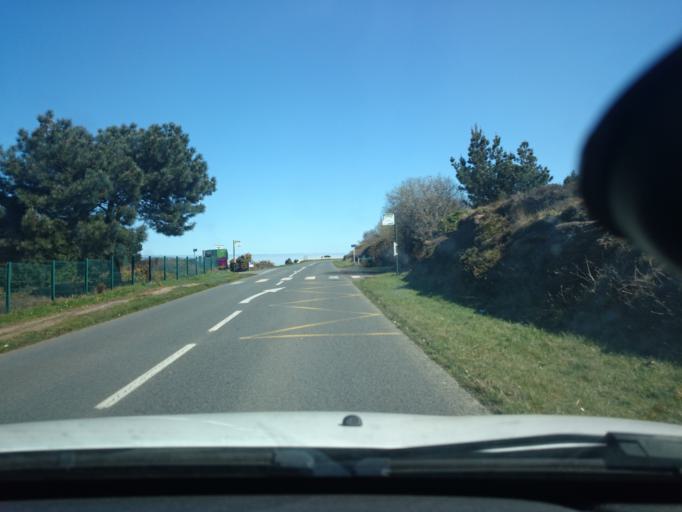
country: FR
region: Brittany
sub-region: Departement des Cotes-d'Armor
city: Tregastel
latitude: 48.8259
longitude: -3.4747
